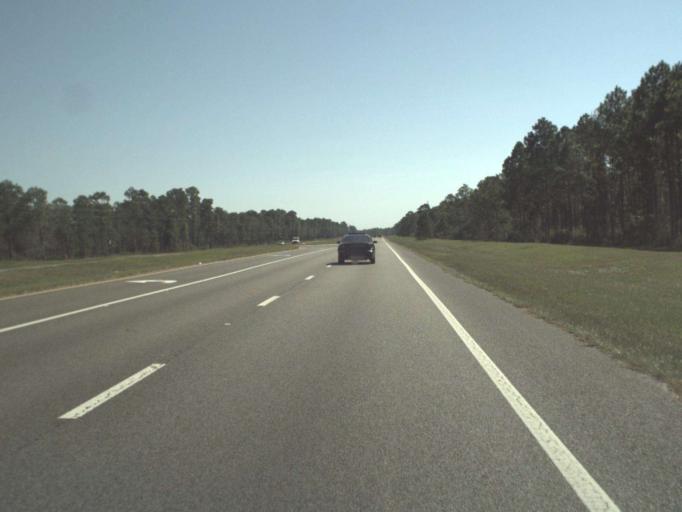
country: US
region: Florida
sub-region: Walton County
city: Seaside
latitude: 30.3634
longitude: -86.1725
